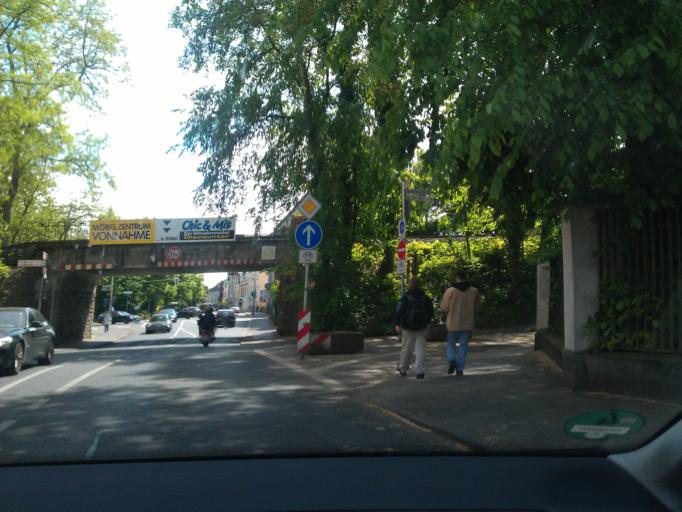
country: DE
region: North Rhine-Westphalia
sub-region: Regierungsbezirk Dusseldorf
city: Hilden
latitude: 51.1642
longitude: 6.9394
